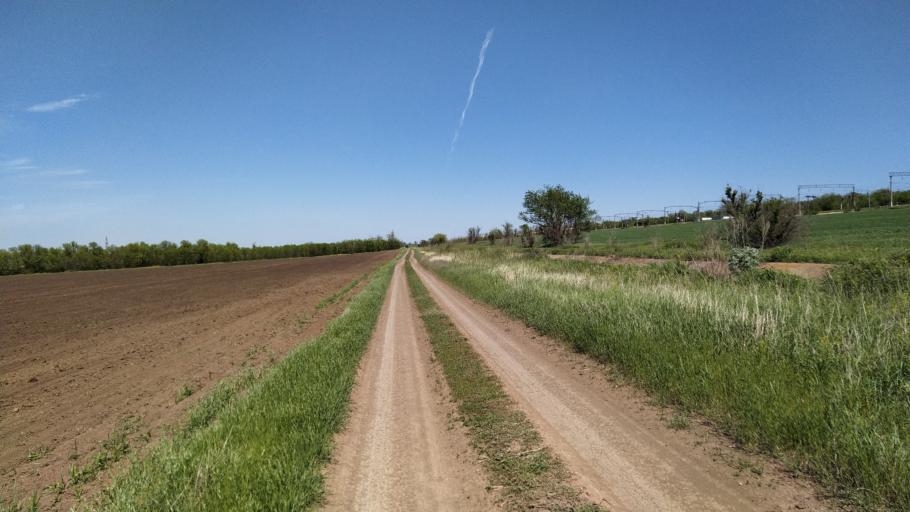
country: RU
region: Rostov
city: Kuleshovka
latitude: 47.0318
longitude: 39.6344
